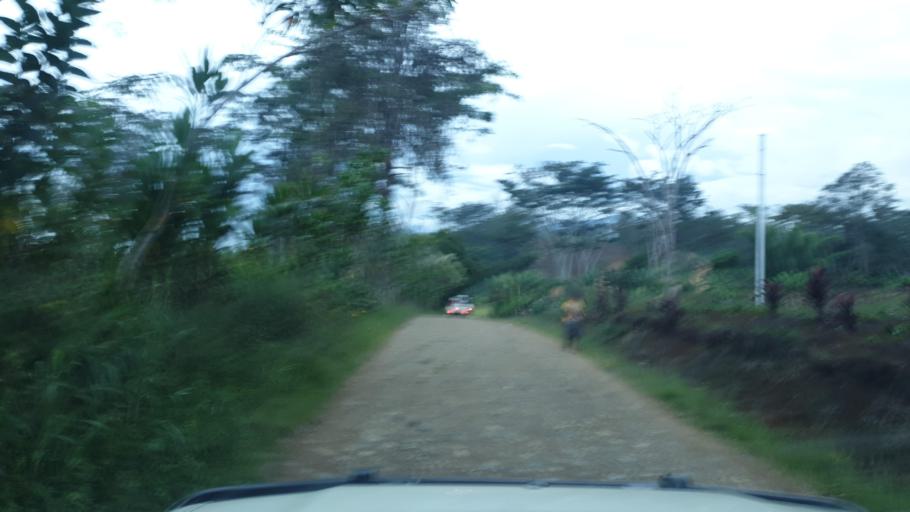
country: PG
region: Eastern Highlands
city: Goroka
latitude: -5.9850
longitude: 145.2828
